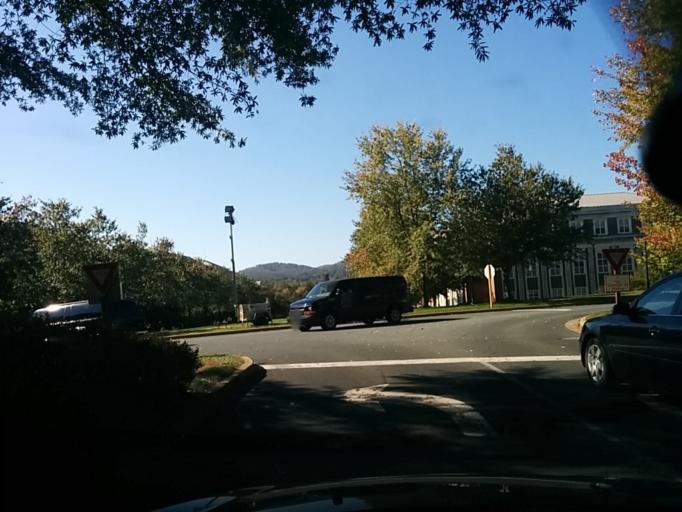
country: US
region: Virginia
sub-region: City of Charlottesville
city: Charlottesville
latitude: 38.0258
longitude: -78.5250
